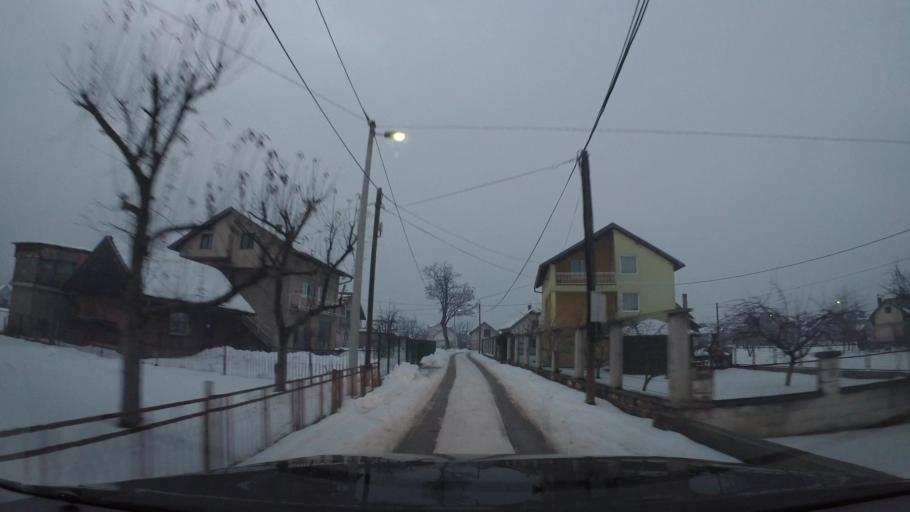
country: BA
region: Federation of Bosnia and Herzegovina
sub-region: Kanton Sarajevo
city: Sarajevo
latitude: 43.8536
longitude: 18.2933
